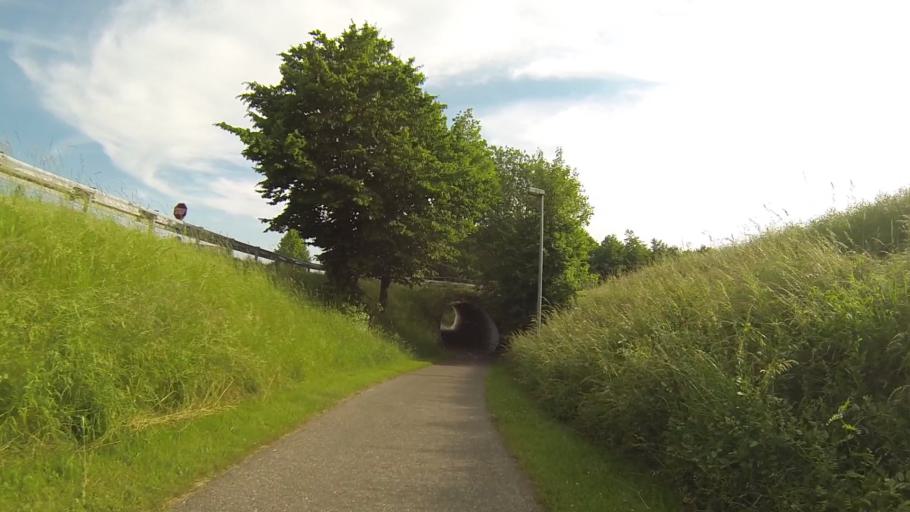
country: DE
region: Baden-Wuerttemberg
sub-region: Tuebingen Region
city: Staig
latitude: 48.3350
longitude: 9.9714
